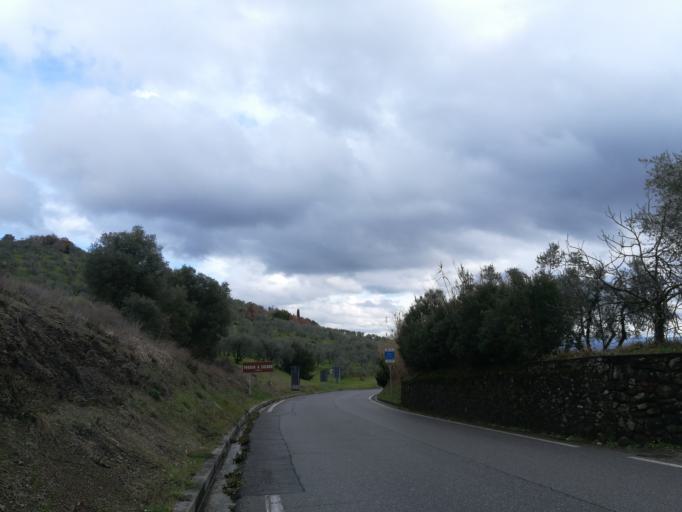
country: IT
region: Tuscany
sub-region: Provincia di Prato
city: Carmignano
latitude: 43.8047
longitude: 11.0316
